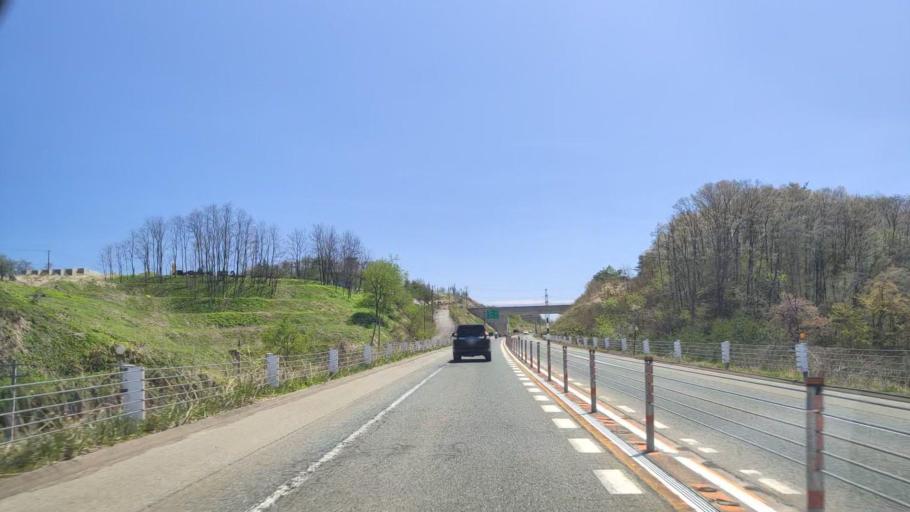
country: JP
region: Yamagata
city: Shinjo
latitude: 38.7246
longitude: 140.3078
